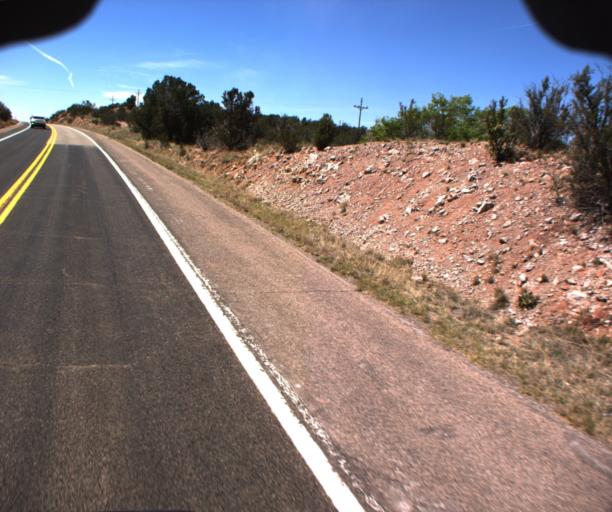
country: US
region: Arizona
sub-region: Mohave County
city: Peach Springs
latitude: 35.5257
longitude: -113.2156
